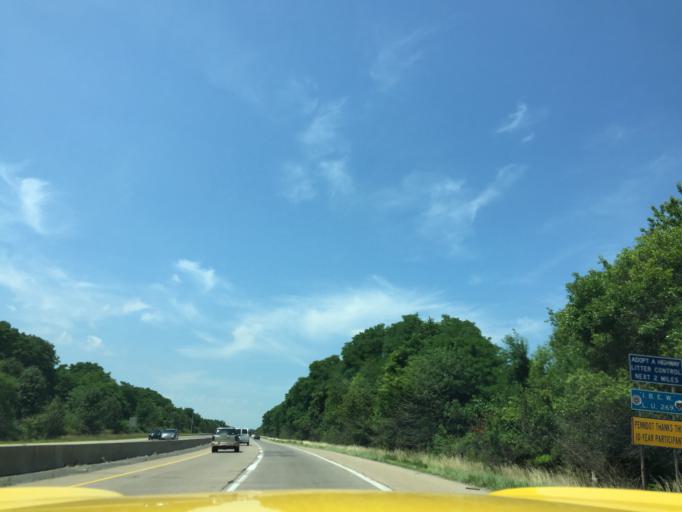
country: US
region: Pennsylvania
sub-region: Bucks County
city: Fairless Hills
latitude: 40.1955
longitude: -74.8320
